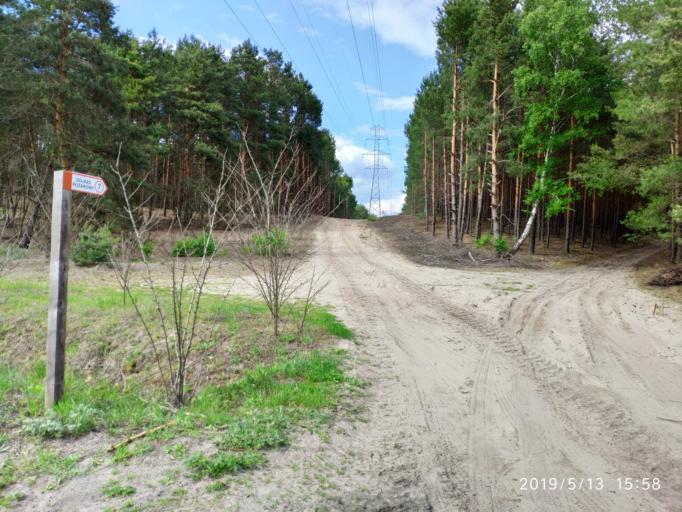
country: PL
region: Lubusz
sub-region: Powiat zielonogorski
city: Czerwiensk
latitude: 52.0038
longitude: 15.4552
